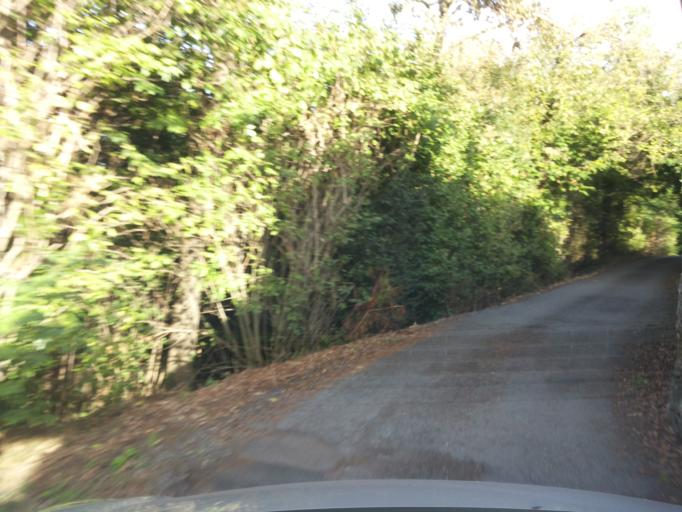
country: IT
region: Piedmont
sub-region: Provincia di Biella
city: Roppolo
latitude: 45.4283
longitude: 8.0756
